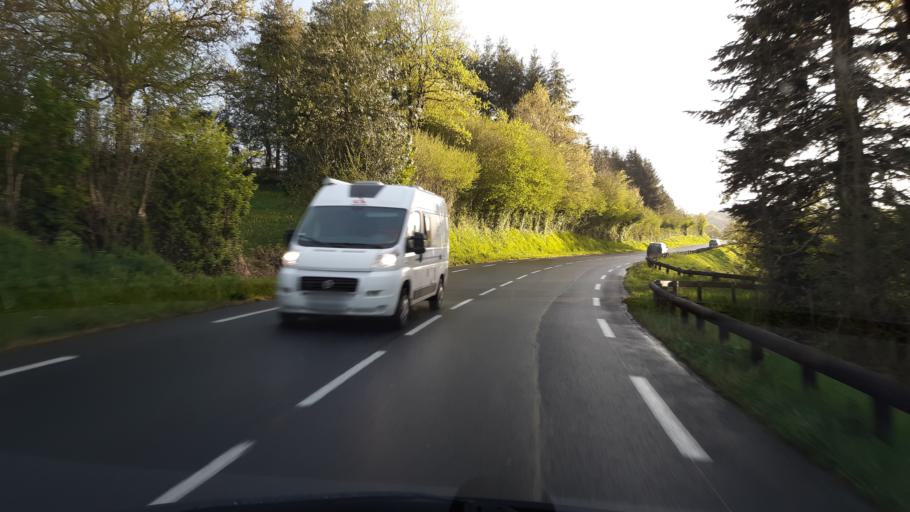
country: FR
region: Lower Normandy
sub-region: Departement de la Manche
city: Agneaux
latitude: 49.0799
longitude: -1.1208
